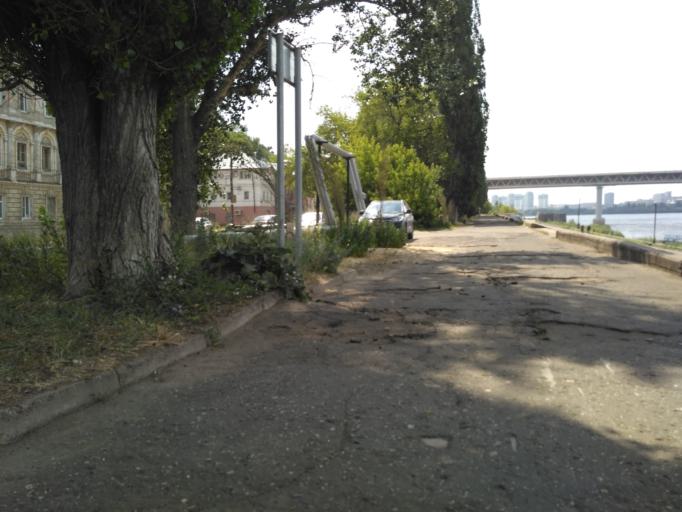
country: RU
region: Nizjnij Novgorod
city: Nizhniy Novgorod
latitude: 56.3218
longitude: 43.9735
